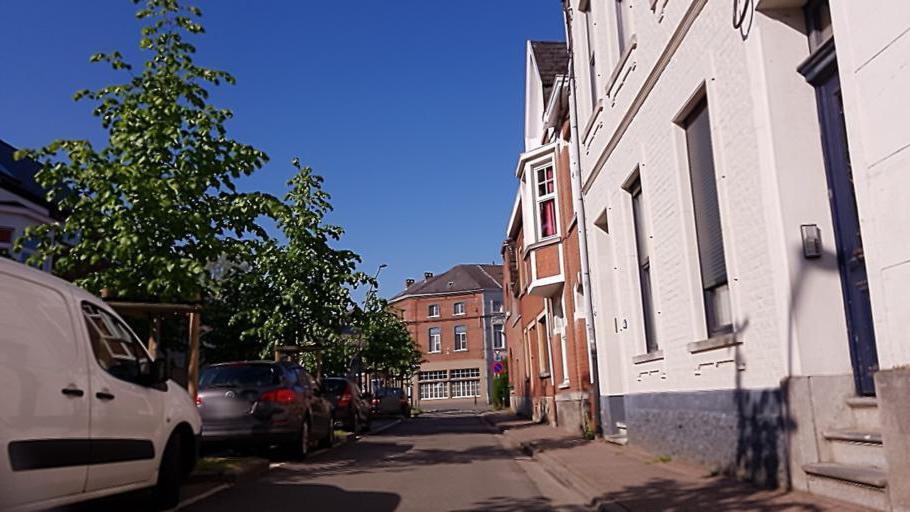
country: BE
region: Wallonia
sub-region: Province du Brabant Wallon
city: Wavre
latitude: 50.7195
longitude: 4.6169
